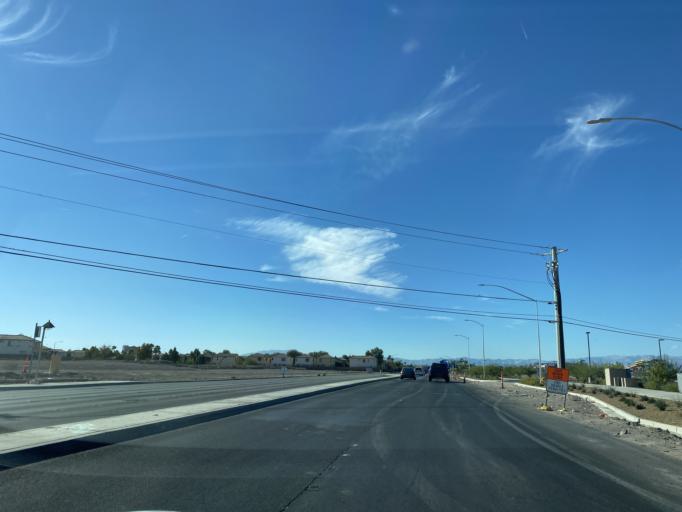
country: US
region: Nevada
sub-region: Clark County
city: Henderson
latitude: 36.0711
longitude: -115.0179
